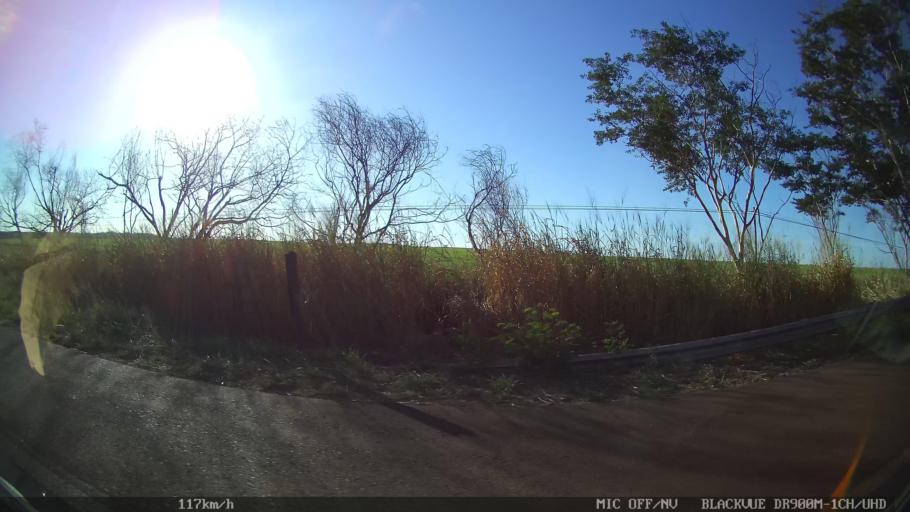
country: BR
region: Sao Paulo
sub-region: Guapiacu
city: Guapiacu
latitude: -20.7383
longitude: -49.0865
